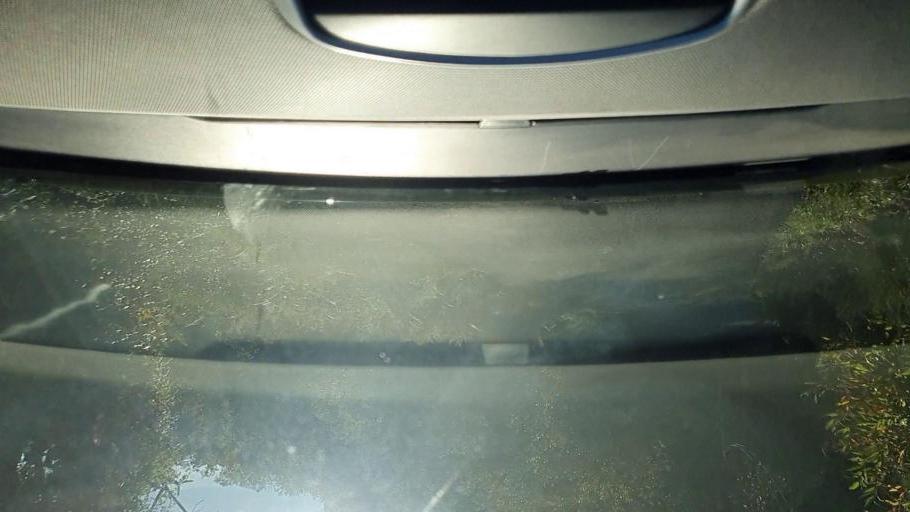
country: FR
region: Languedoc-Roussillon
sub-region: Departement du Gard
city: Sumene
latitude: 44.0245
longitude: 3.7619
